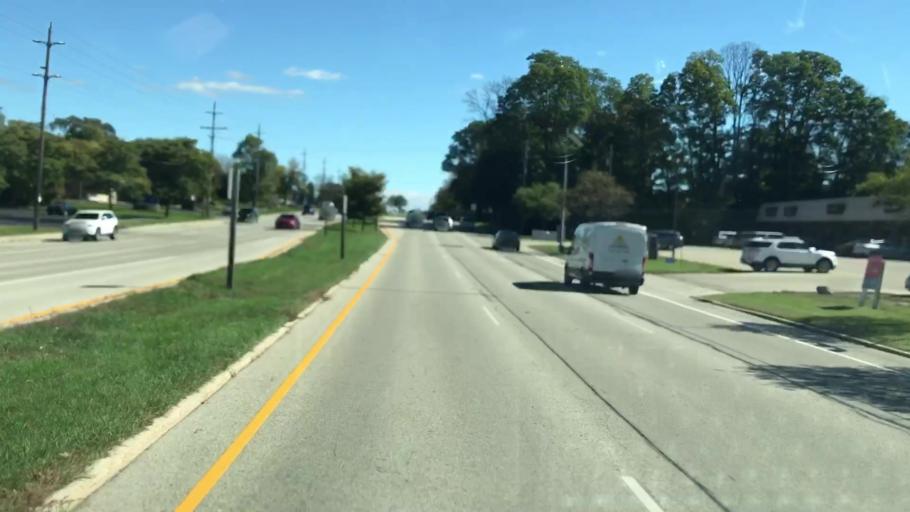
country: US
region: Wisconsin
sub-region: Waukesha County
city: Butler
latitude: 43.0895
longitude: -88.0826
